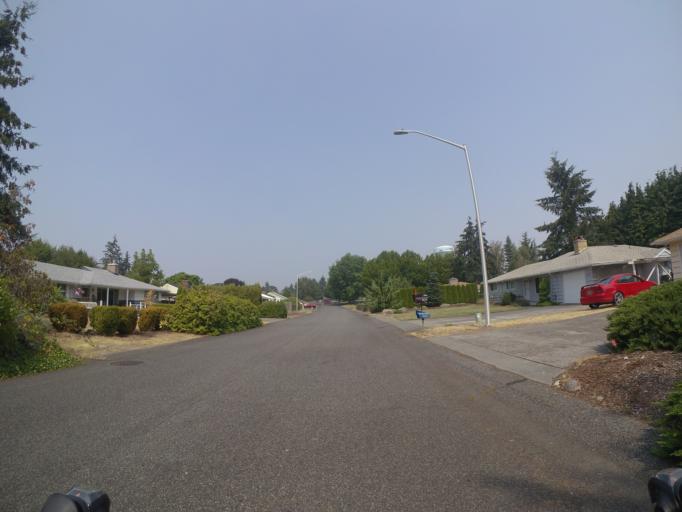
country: US
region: Washington
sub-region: Pierce County
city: Lakewood
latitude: 47.1605
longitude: -122.5068
